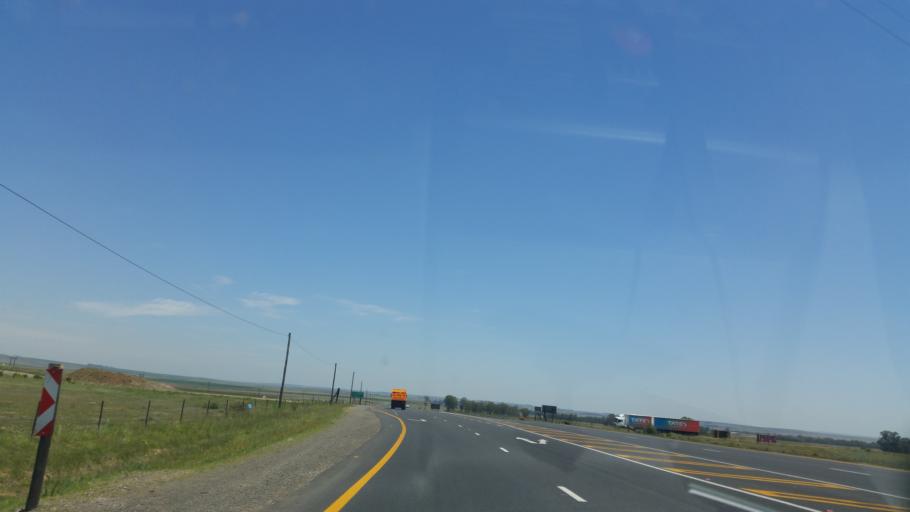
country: ZA
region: Orange Free State
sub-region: Thabo Mofutsanyana District Municipality
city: Harrismith
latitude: -28.2408
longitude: 29.1212
